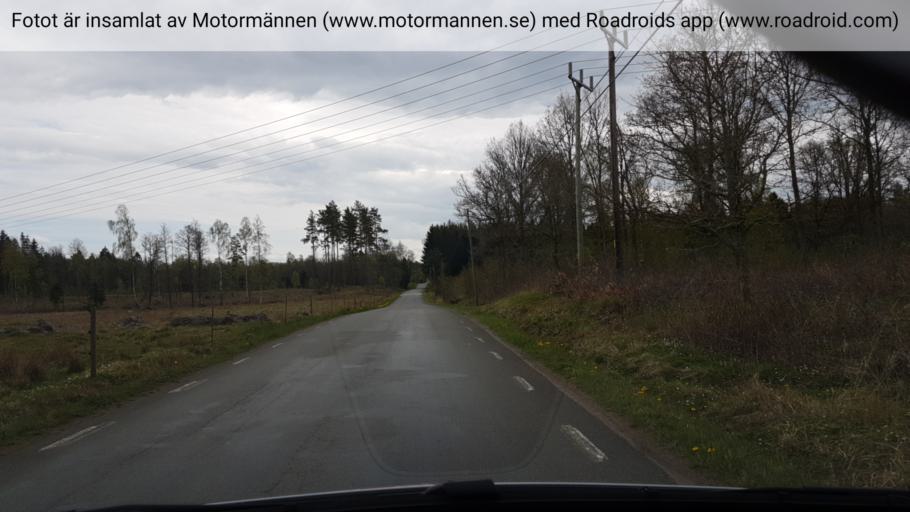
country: SE
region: Vaestra Goetaland
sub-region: Skara Kommun
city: Skara
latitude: 58.3761
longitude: 13.4736
